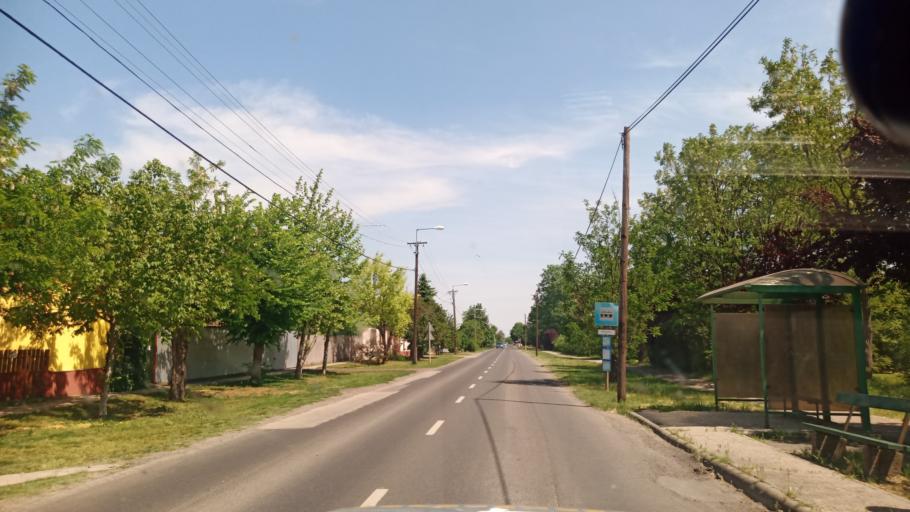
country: HU
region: Bekes
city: Oroshaza
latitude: 46.5625
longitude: 20.6128
